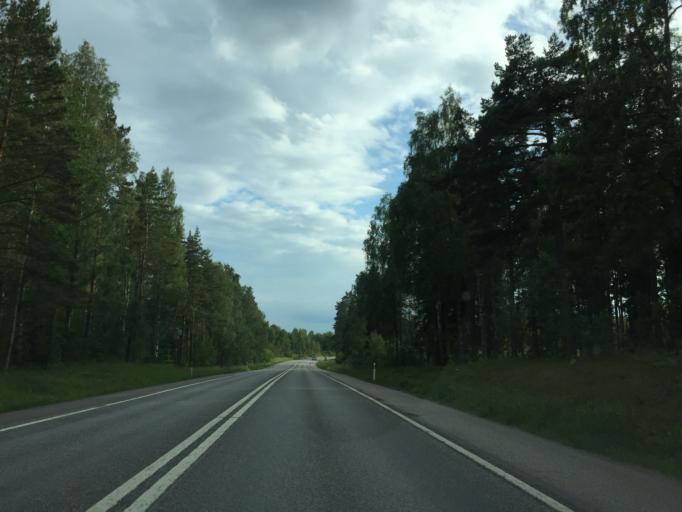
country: SE
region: OErebro
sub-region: Lindesbergs Kommun
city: Fellingsbro
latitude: 59.3657
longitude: 15.6972
